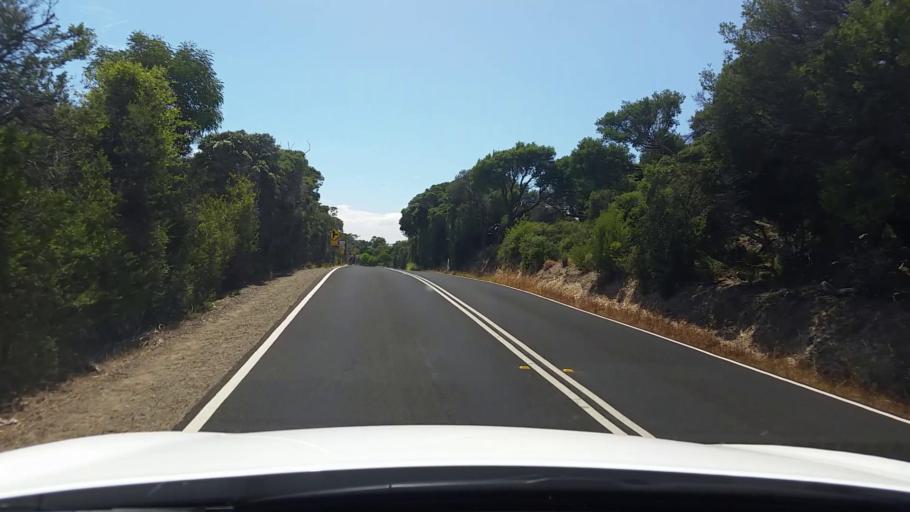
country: AU
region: Victoria
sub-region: Mornington Peninsula
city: Mount Martha
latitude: -38.2793
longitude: 144.9988
